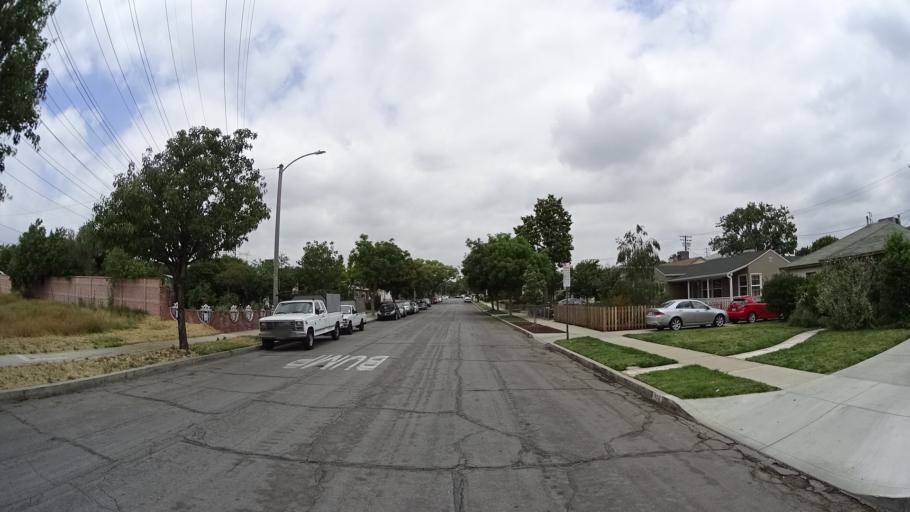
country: US
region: California
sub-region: Los Angeles County
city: Universal City
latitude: 34.1657
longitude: -118.3471
